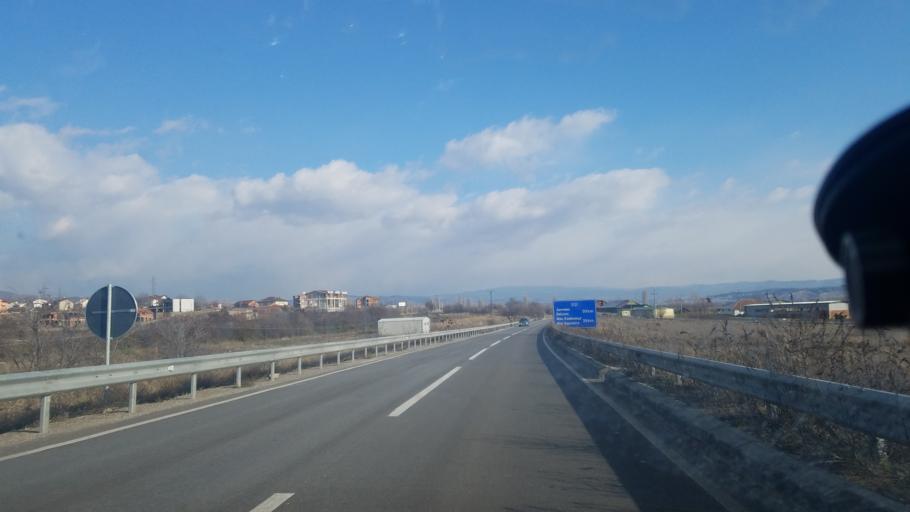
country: MK
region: Kocani
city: Kochani
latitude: 41.9028
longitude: 22.3936
